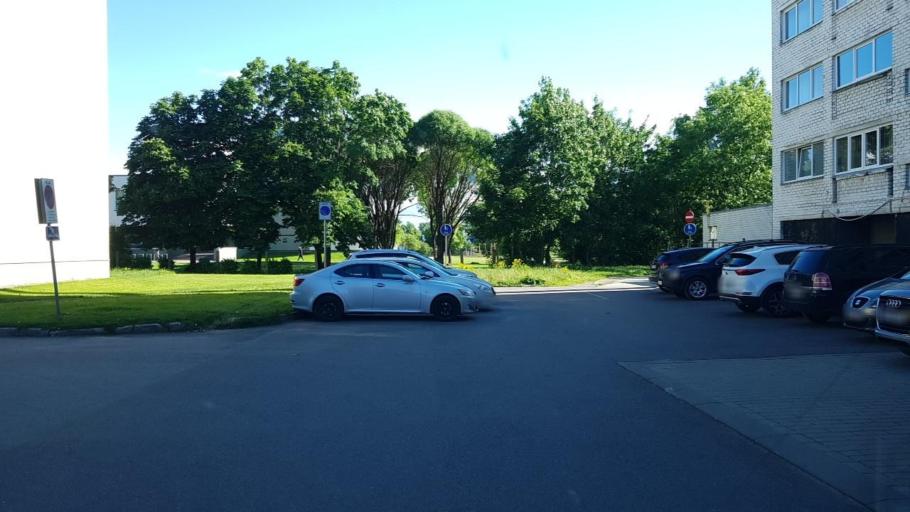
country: EE
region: Ida-Virumaa
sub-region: Narva linn
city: Narva
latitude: 59.3799
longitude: 28.1705
